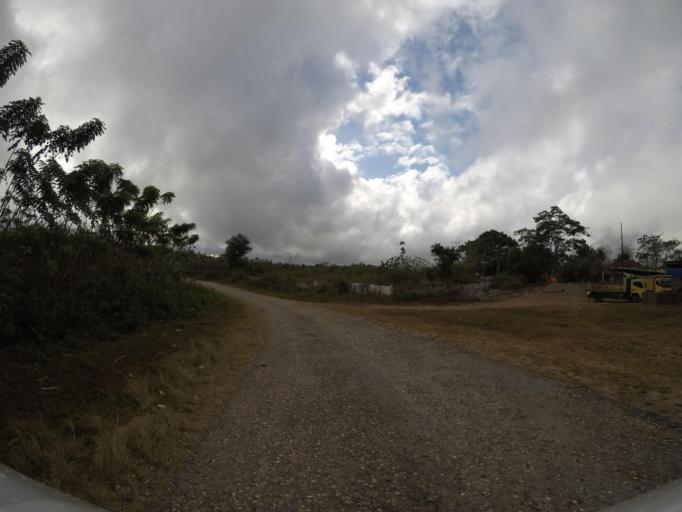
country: TL
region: Lautem
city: Lospalos
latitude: -8.5303
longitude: 126.9846
